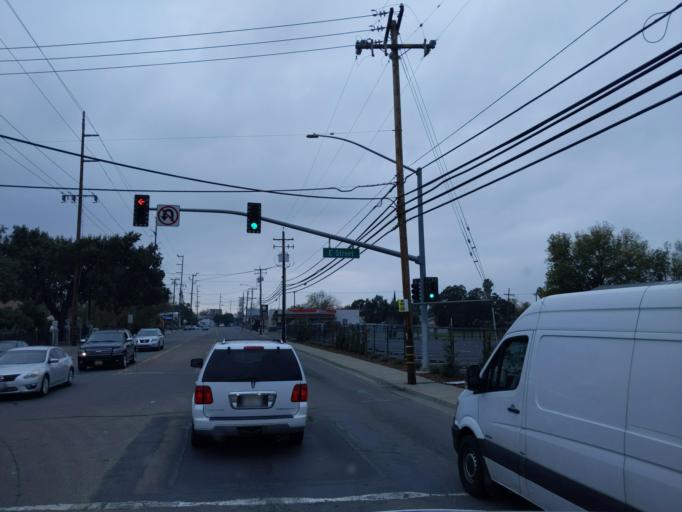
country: US
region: California
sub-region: San Joaquin County
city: August
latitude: 37.9639
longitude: -121.2602
